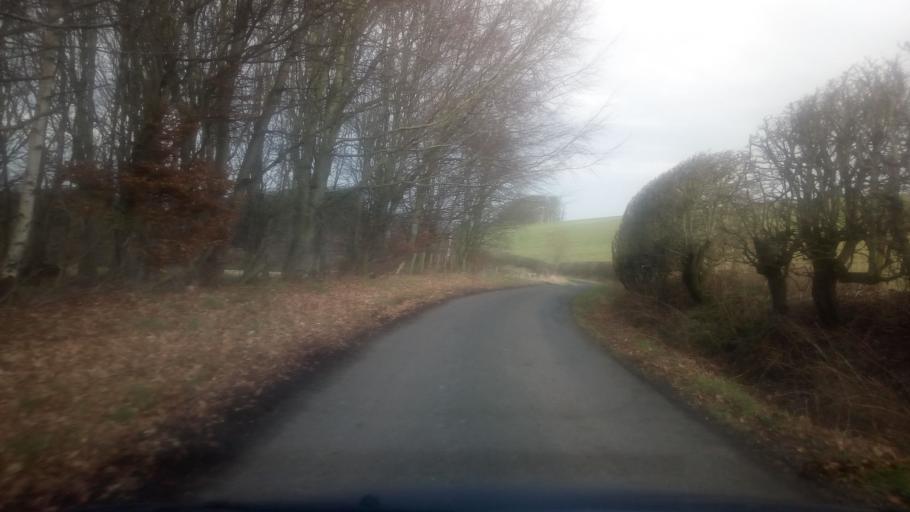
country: GB
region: Scotland
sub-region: The Scottish Borders
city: Jedburgh
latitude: 55.4438
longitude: -2.6313
